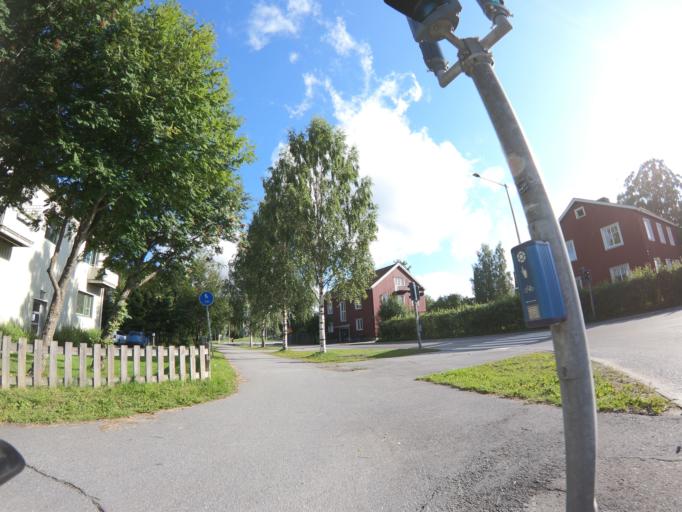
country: SE
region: Vaesterbotten
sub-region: Umea Kommun
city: Umea
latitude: 63.8274
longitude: 20.2853
